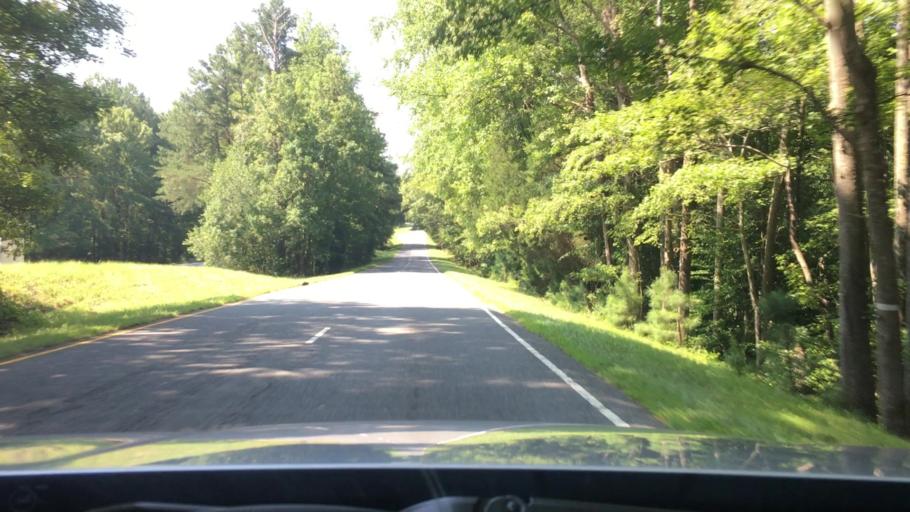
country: US
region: Virginia
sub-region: Caroline County
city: Bowling Green
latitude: 37.9531
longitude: -77.4429
